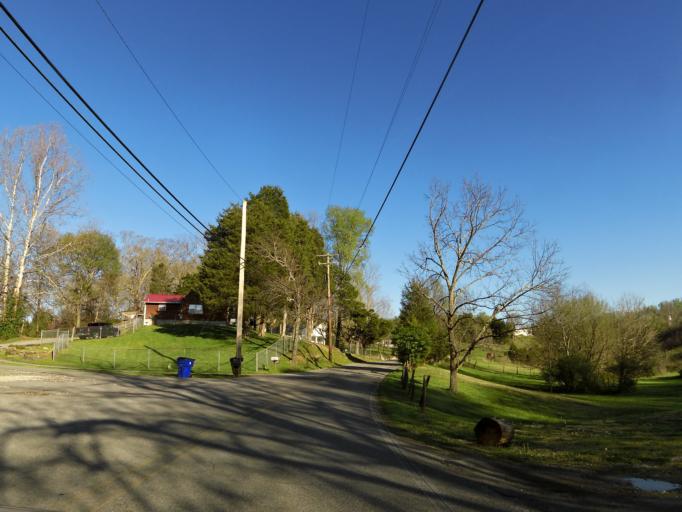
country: US
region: Tennessee
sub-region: Knox County
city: Knoxville
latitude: 35.9731
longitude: -83.8388
